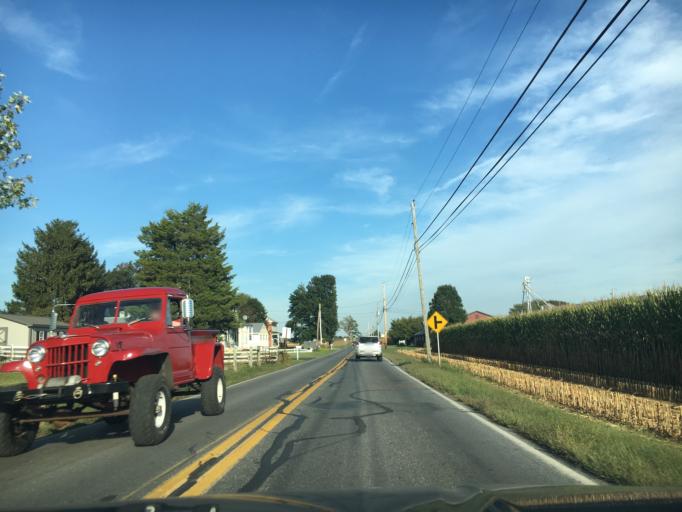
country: US
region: Pennsylvania
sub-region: Lancaster County
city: Brownstown
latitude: 40.1227
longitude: -76.1805
